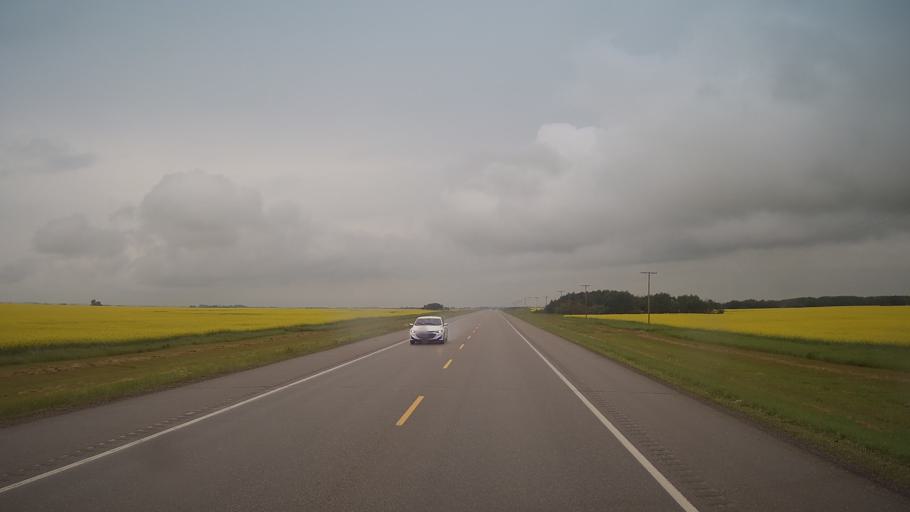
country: CA
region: Saskatchewan
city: Wilkie
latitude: 52.4251
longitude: -108.9066
